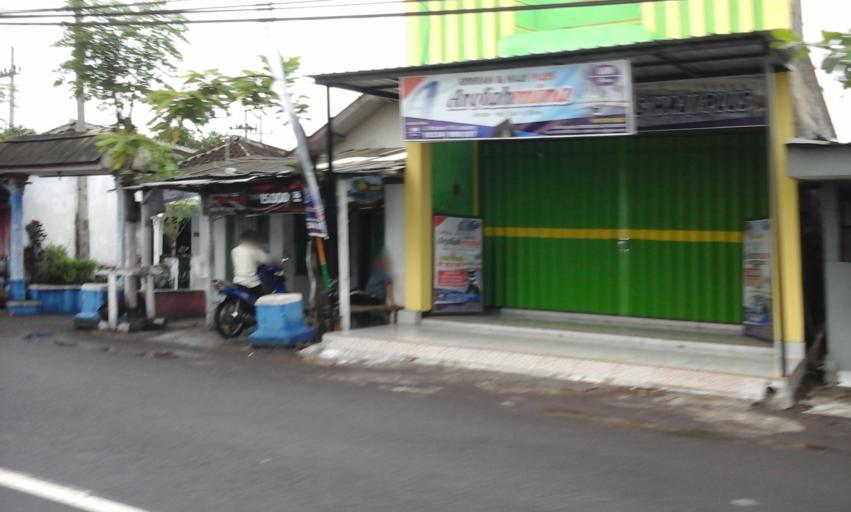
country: ID
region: East Java
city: Pandanwangi
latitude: -8.1440
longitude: 113.2363
